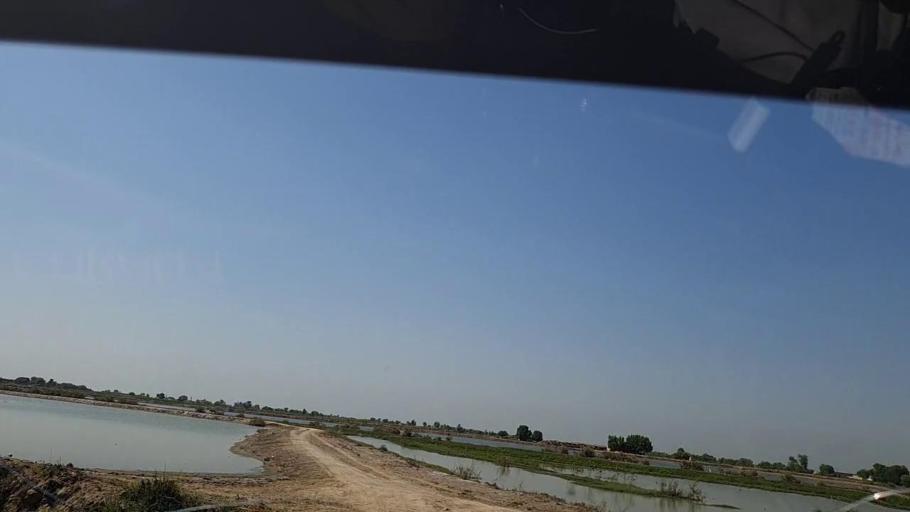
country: PK
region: Sindh
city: Tangwani
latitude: 28.3252
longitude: 69.0863
